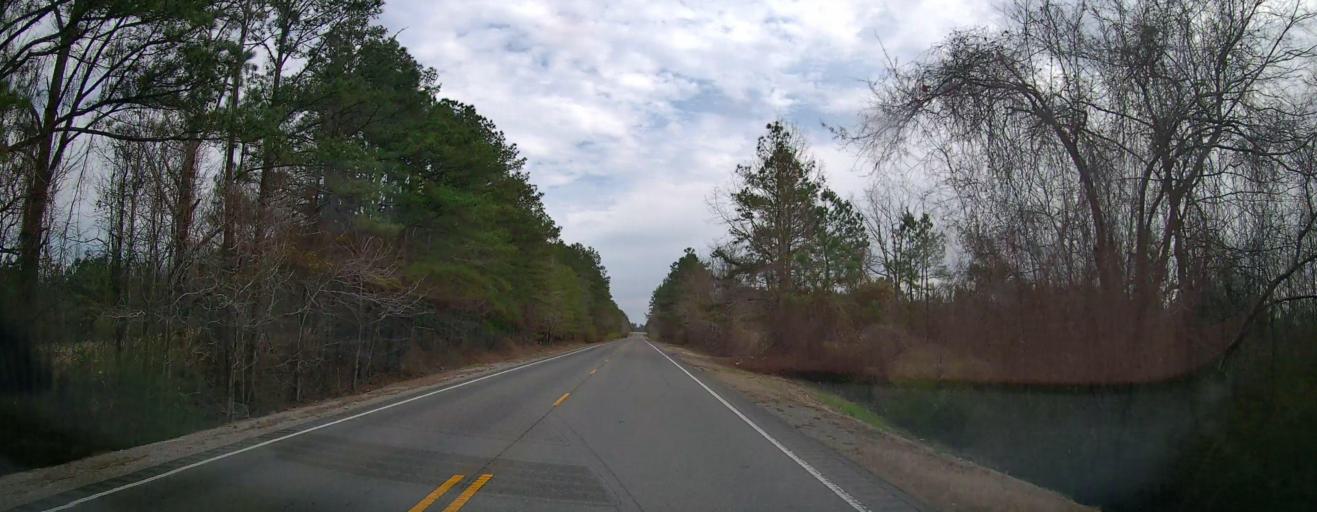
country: US
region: Alabama
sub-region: Marion County
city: Guin
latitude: 34.0453
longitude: -87.9593
